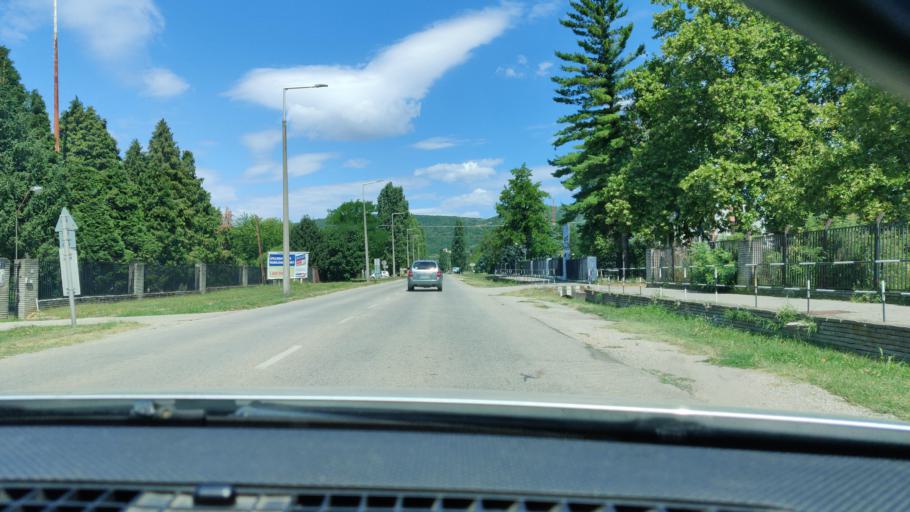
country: HU
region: Baranya
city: Siklos
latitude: 45.8642
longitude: 18.2857
